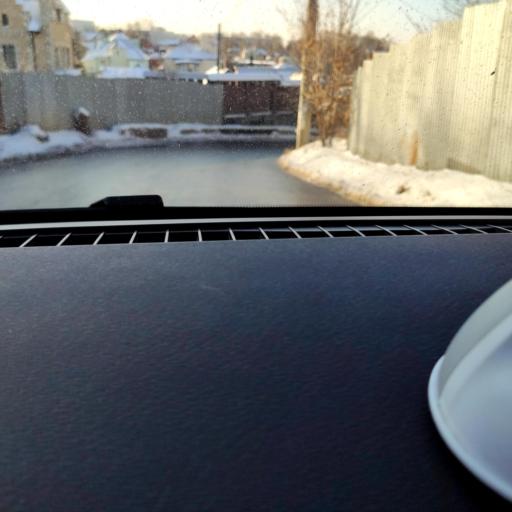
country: RU
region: Samara
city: Samara
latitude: 53.2777
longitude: 50.1984
